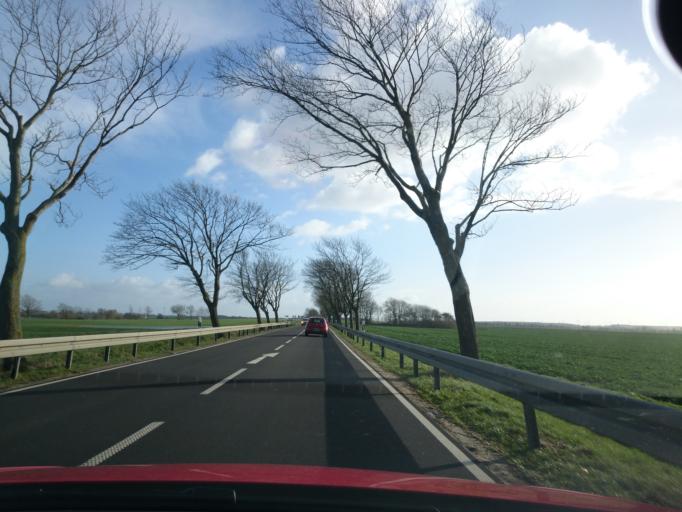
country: DE
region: Mecklenburg-Vorpommern
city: Barth
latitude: 54.3300
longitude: 12.7221
